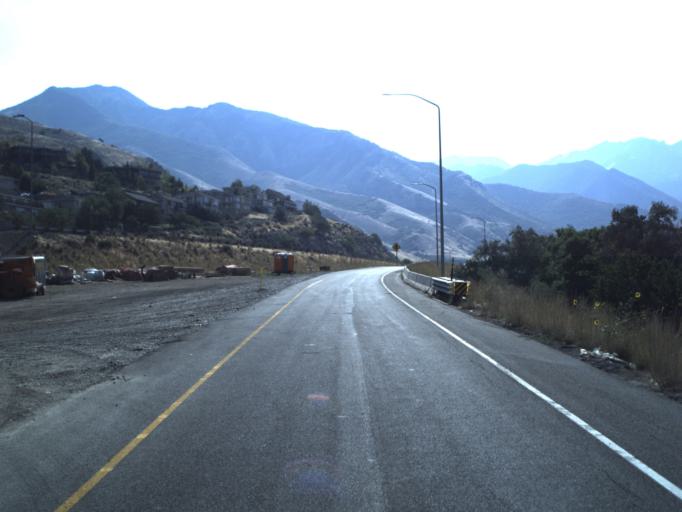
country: US
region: Utah
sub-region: Salt Lake County
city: Canyon Rim
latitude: 40.7168
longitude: -111.8103
